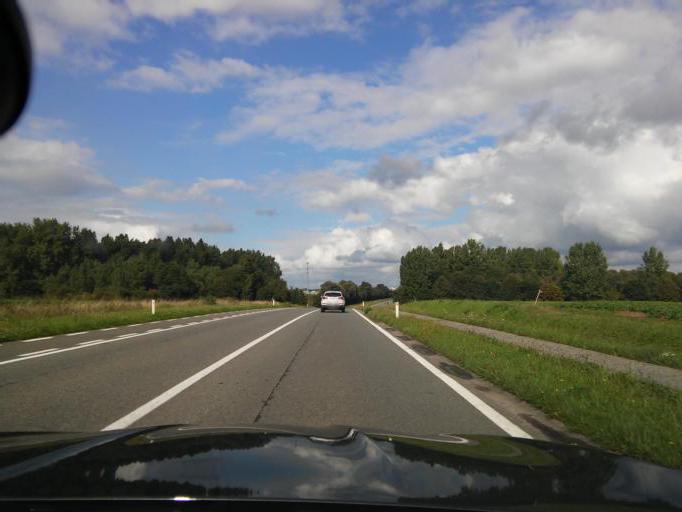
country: BE
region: Flanders
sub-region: Provincie Oost-Vlaanderen
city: Ninove
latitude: 50.8220
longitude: 3.9607
